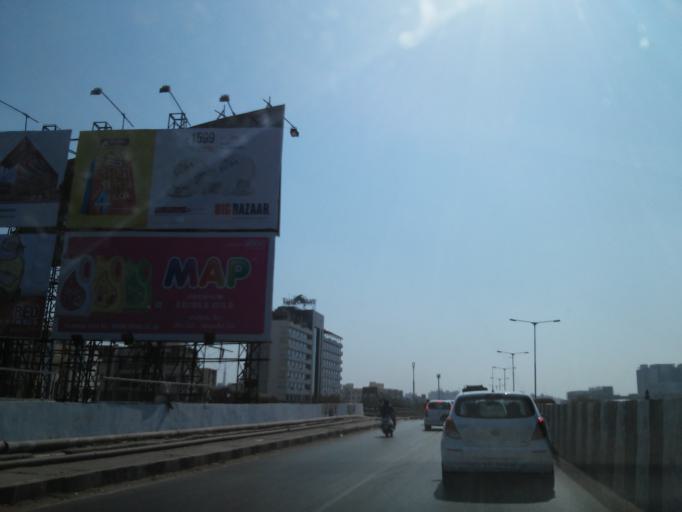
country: IN
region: Gujarat
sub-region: Ahmadabad
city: Ahmedabad
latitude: 23.0667
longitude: 72.5224
